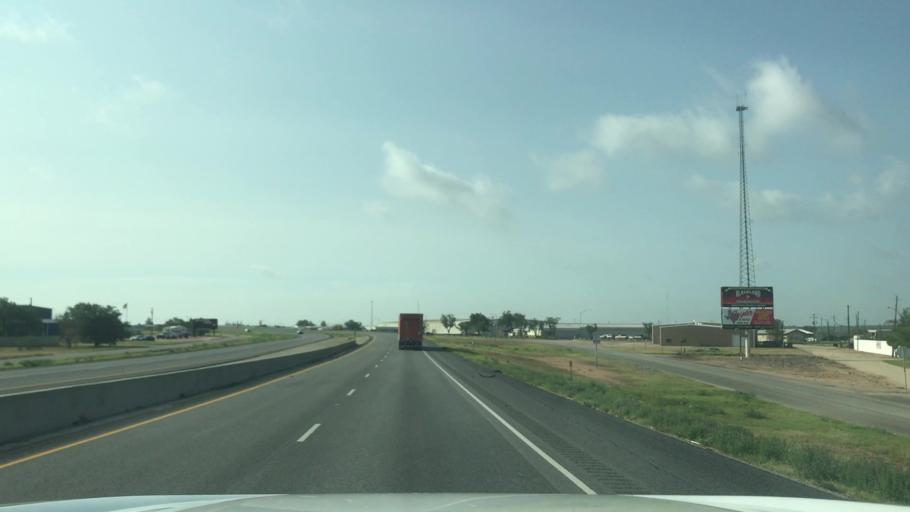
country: US
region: Texas
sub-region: Scurry County
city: Snyder
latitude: 32.7450
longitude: -100.9233
